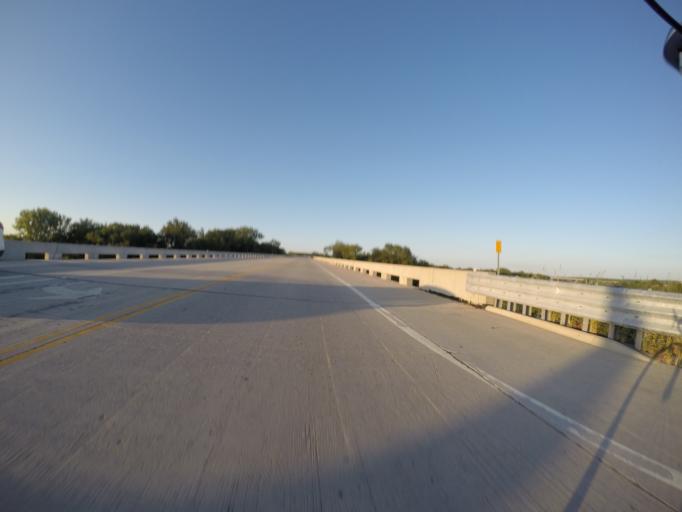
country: US
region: Kansas
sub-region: Riley County
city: Ogden
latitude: 39.1179
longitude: -96.7001
